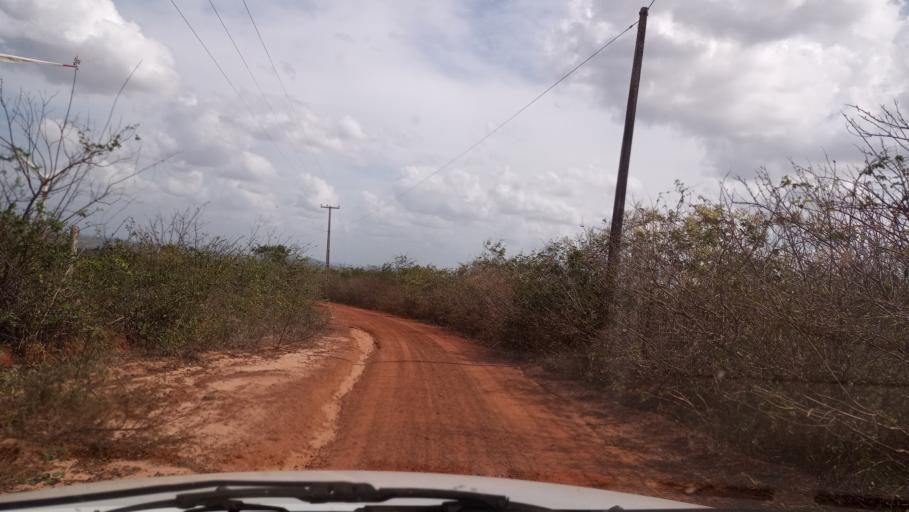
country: BR
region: Rio Grande do Norte
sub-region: Joao Camara
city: Joao Camara
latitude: -5.4199
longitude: -35.8568
